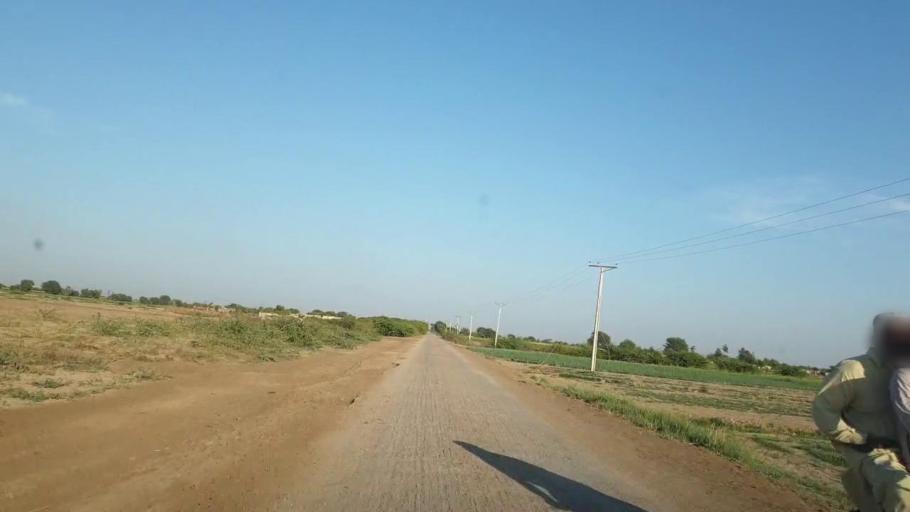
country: PK
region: Sindh
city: Kunri
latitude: 25.0910
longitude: 69.4378
